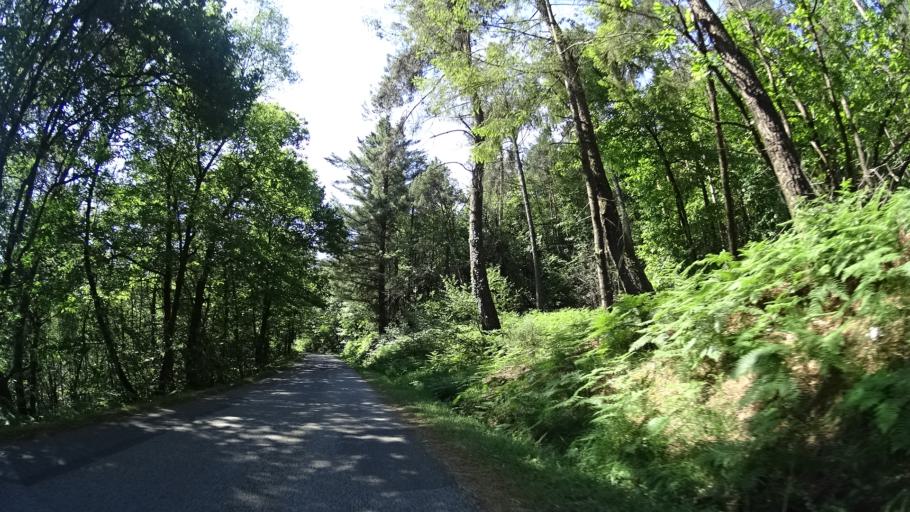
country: FR
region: Brittany
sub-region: Departement d'Ille-et-Vilaine
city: Langon
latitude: 47.7656
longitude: -1.8489
